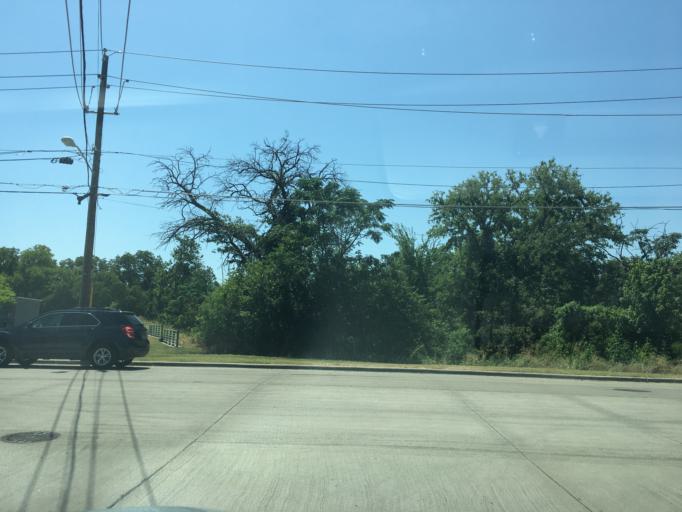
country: US
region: Texas
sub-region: Dallas County
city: Highland Park
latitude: 32.8467
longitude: -96.7458
